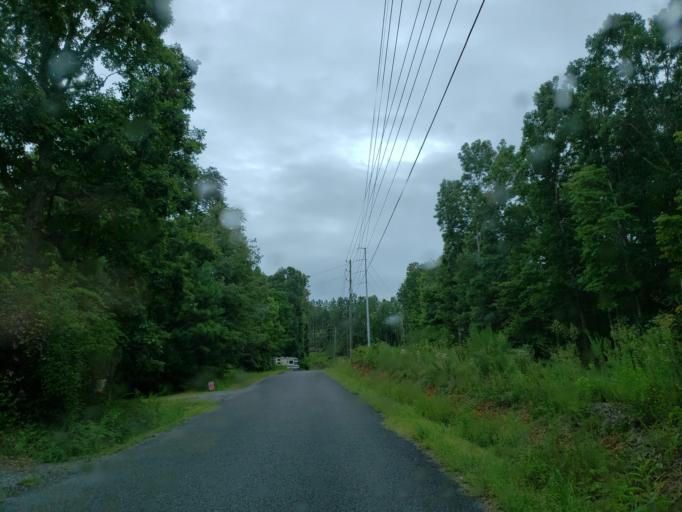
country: US
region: Georgia
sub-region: Gilmer County
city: Ellijay
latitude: 34.6199
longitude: -84.5773
